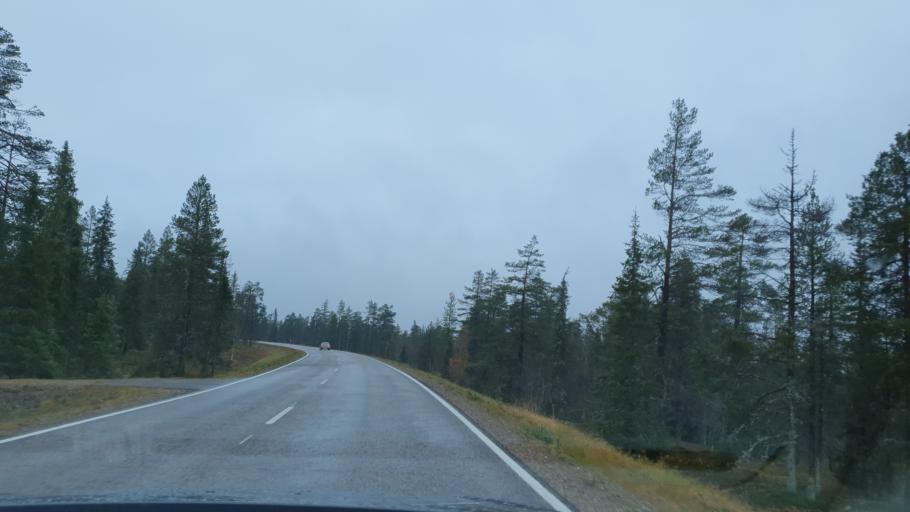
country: FI
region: Lapland
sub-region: Tunturi-Lappi
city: Kolari
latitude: 67.5711
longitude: 24.1781
